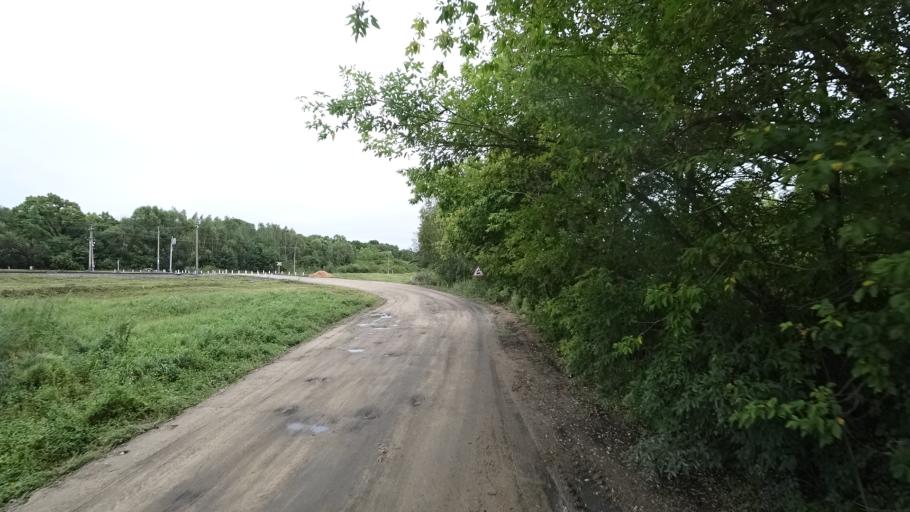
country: RU
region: Primorskiy
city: Rettikhovka
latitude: 44.1635
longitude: 132.7403
